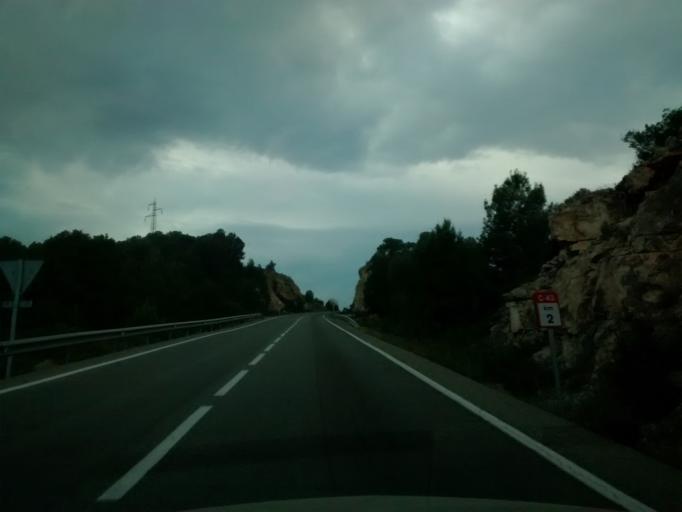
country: ES
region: Catalonia
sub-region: Provincia de Tarragona
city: Benifallet
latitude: 40.9958
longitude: 0.5162
